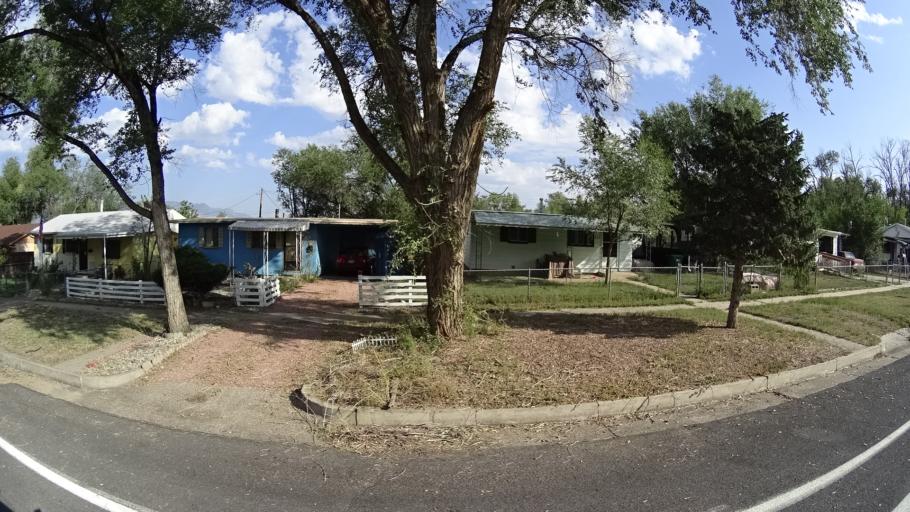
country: US
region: Colorado
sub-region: El Paso County
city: Colorado Springs
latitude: 38.8228
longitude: -104.8121
